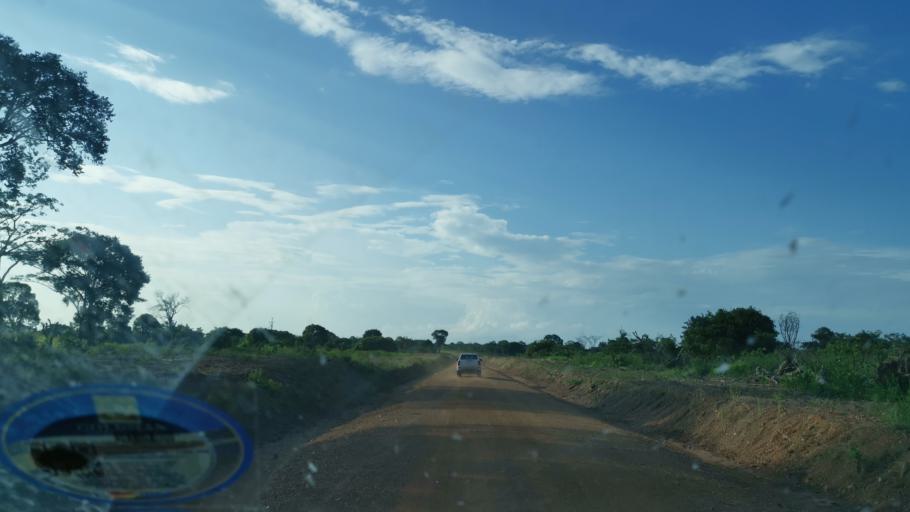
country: ZM
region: Luapula
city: Samfya
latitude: -11.1094
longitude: 29.5757
